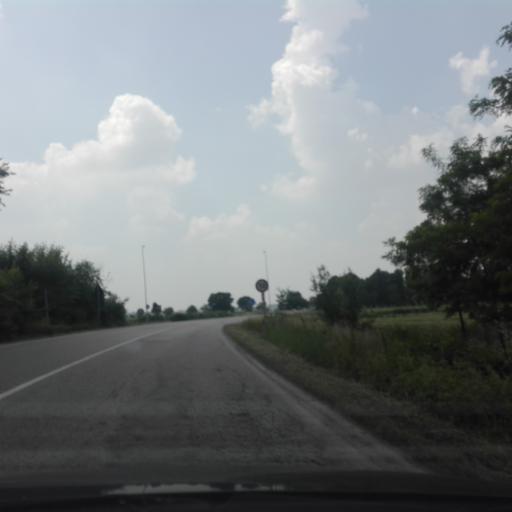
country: IT
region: Veneto
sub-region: Provincia di Rovigo
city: Villanova Marchesana
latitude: 44.9879
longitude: 11.9420
